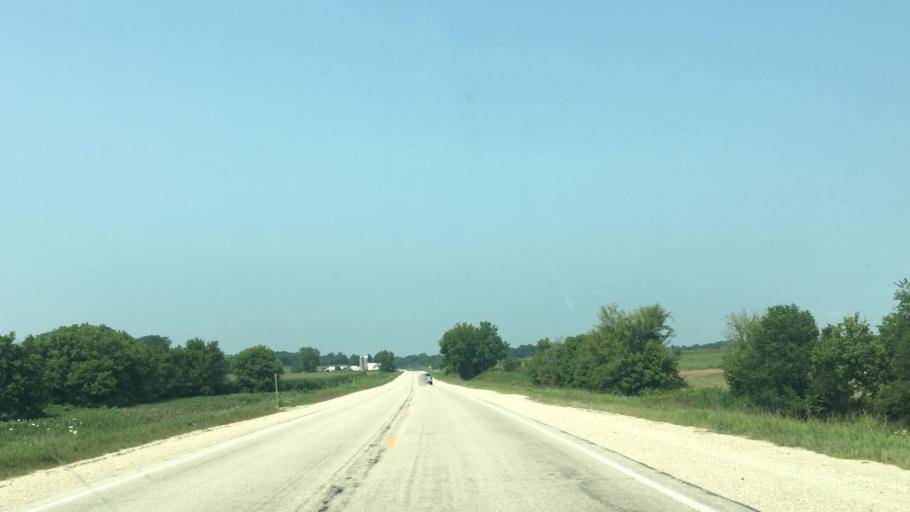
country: US
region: Iowa
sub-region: Fayette County
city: West Union
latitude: 43.0543
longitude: -91.8392
